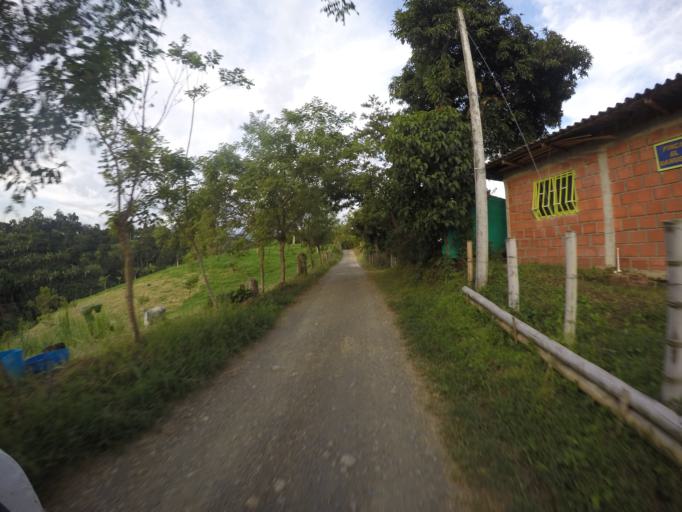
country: CO
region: Valle del Cauca
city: Ulloa
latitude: 4.7134
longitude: -75.7230
